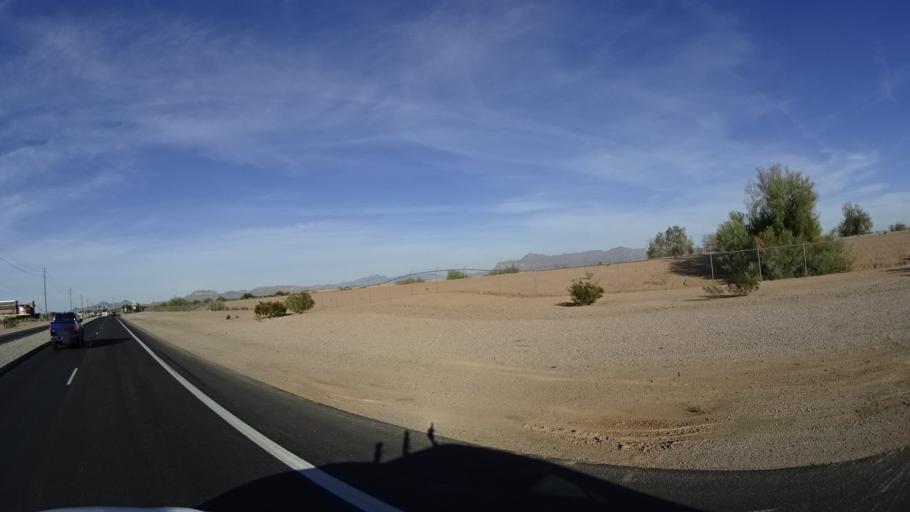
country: US
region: Arizona
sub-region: Maricopa County
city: Queen Creek
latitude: 33.3468
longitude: -111.6356
